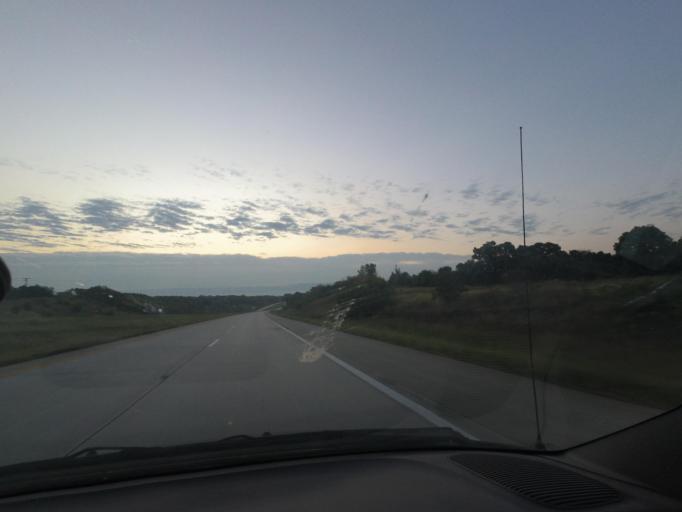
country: US
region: Missouri
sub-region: Linn County
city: Marceline
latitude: 39.7651
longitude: -92.7402
